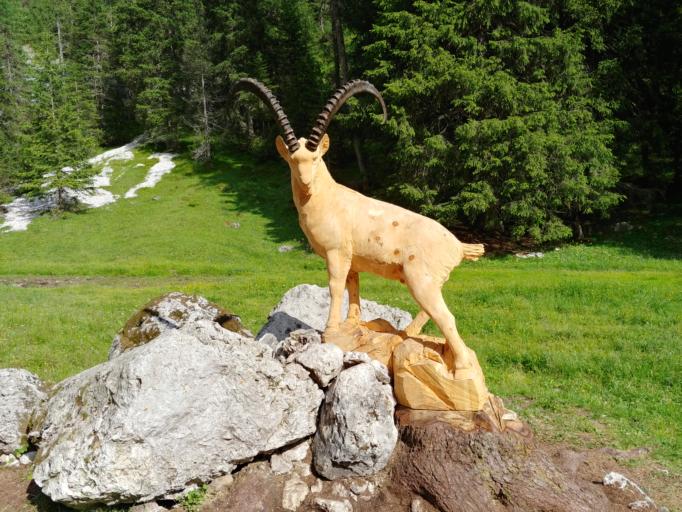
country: IT
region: Trentino-Alto Adige
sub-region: Bolzano
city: Selva
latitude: 46.5652
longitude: 11.7810
